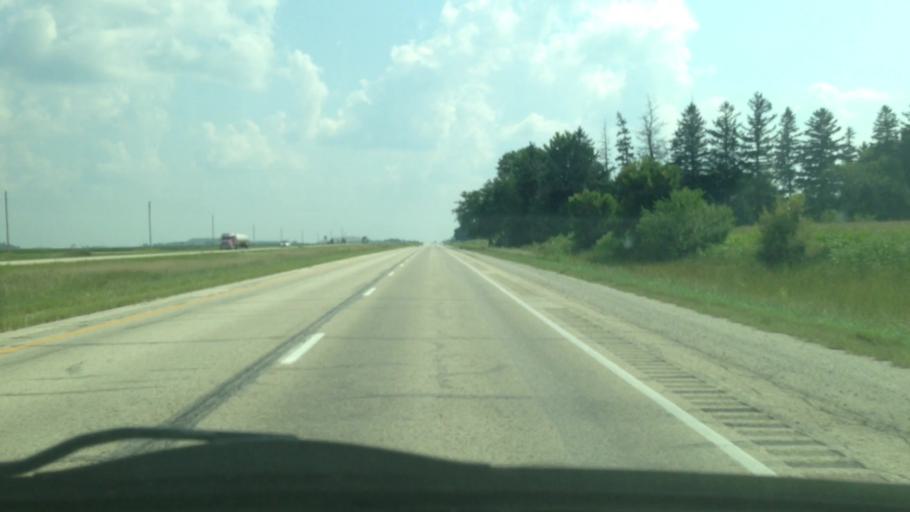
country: US
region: Iowa
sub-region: Bremer County
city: Tripoli
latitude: 42.8566
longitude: -92.3376
